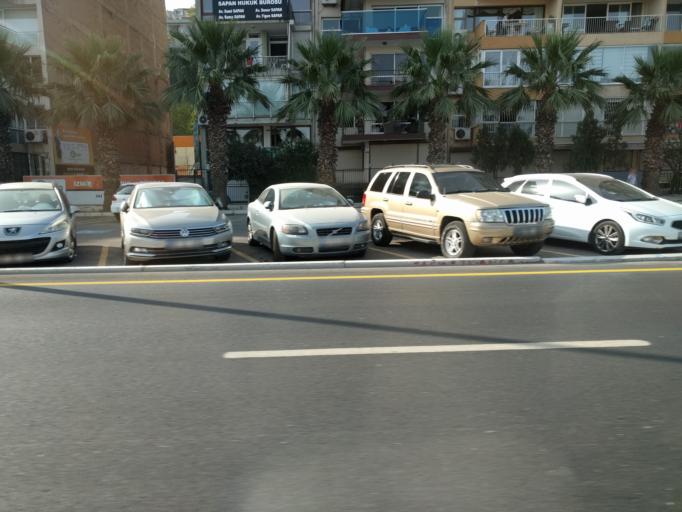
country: TR
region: Izmir
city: Izmir
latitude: 38.4100
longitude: 27.1173
